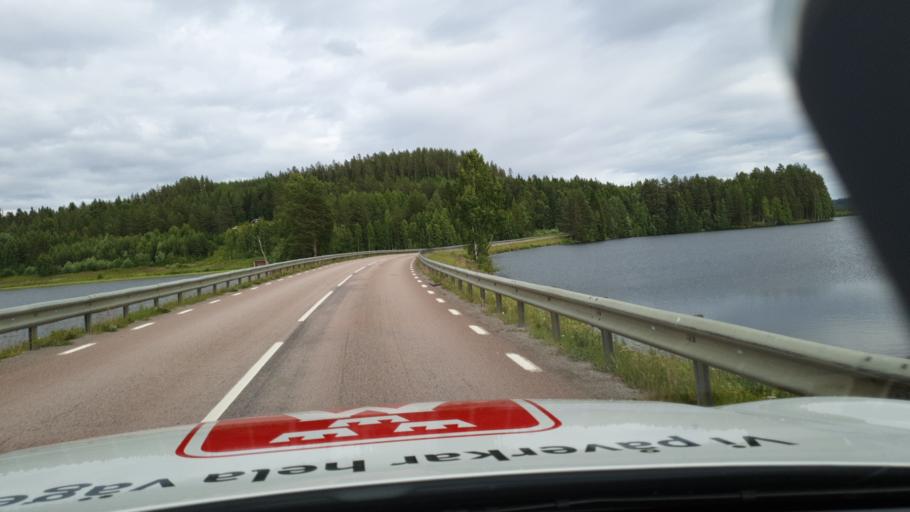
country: SE
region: Vaesternorrland
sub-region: Solleftea Kommun
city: As
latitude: 63.6002
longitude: 16.2203
